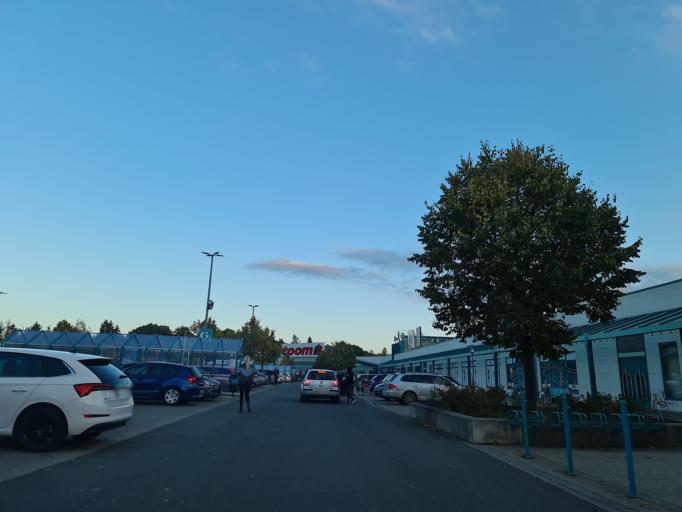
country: DE
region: Saxony
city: Syrau
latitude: 50.5320
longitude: 12.1050
